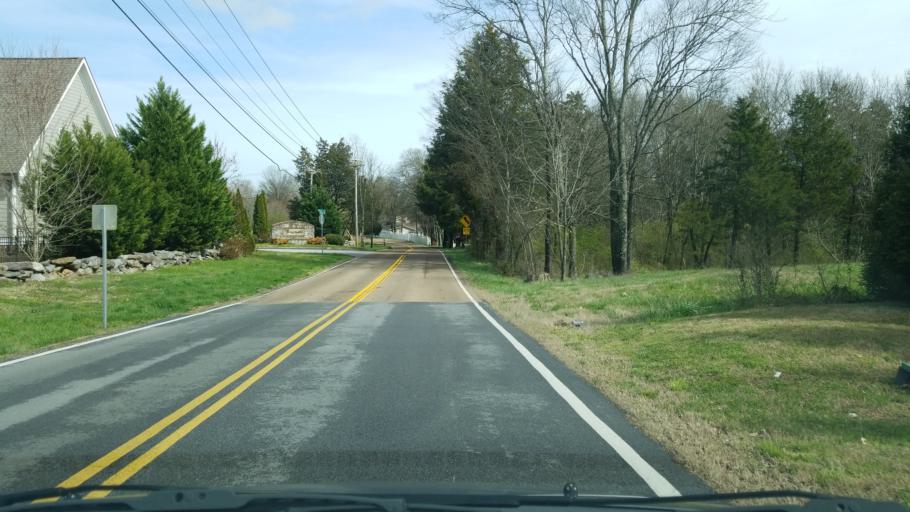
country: US
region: Tennessee
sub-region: Hamilton County
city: Harrison
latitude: 35.1481
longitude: -85.0619
